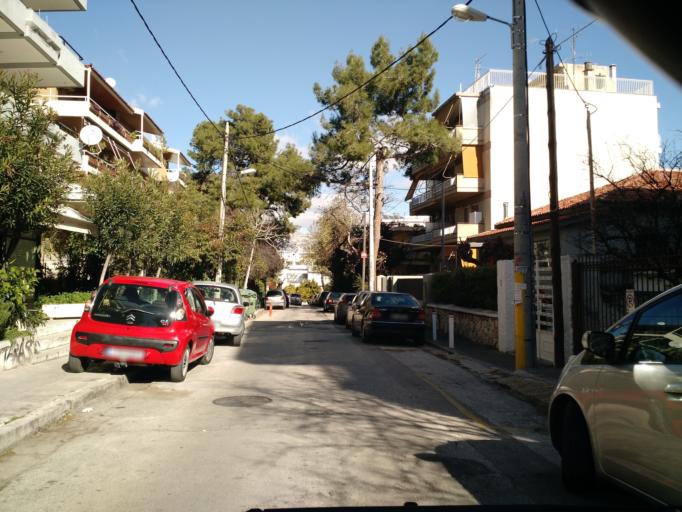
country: GR
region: Attica
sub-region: Nomarchia Athinas
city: Agia Paraskevi
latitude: 38.0053
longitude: 23.8230
